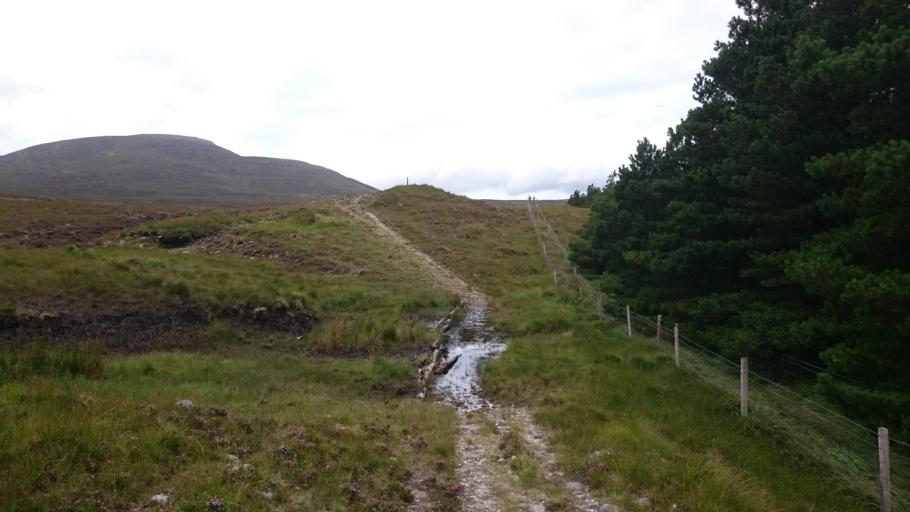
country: IE
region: Connaught
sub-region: Maigh Eo
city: Westport
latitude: 54.0026
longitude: -9.6146
